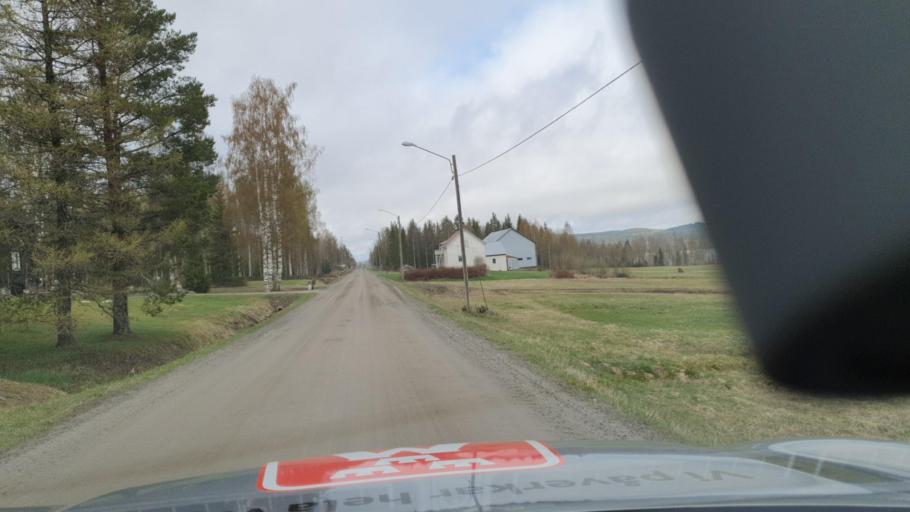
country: SE
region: Vaesterbotten
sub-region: Bjurholms Kommun
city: Bjurholm
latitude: 63.6524
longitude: 19.0429
